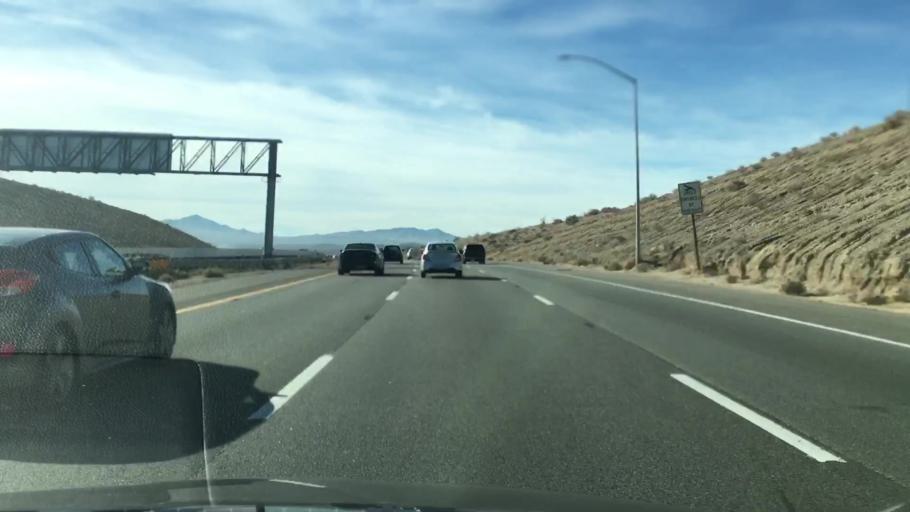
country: US
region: California
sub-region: San Bernardino County
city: Lenwood
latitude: 34.8660
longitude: -117.0814
